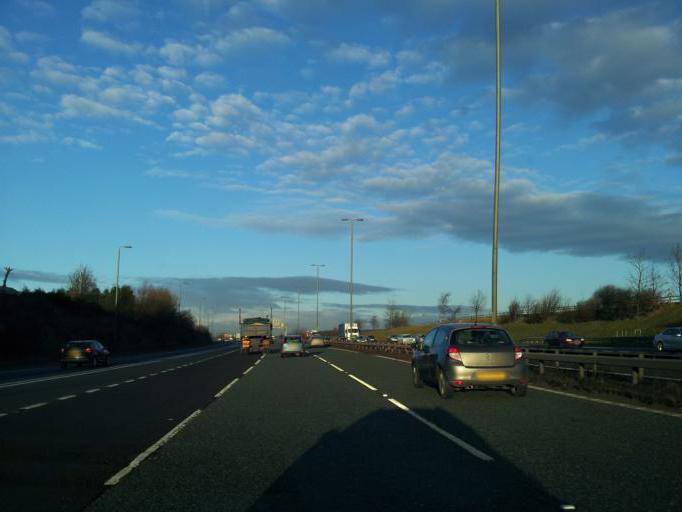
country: GB
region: England
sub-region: City and Borough of Leeds
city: Lofthouse
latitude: 53.7337
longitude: -1.5263
